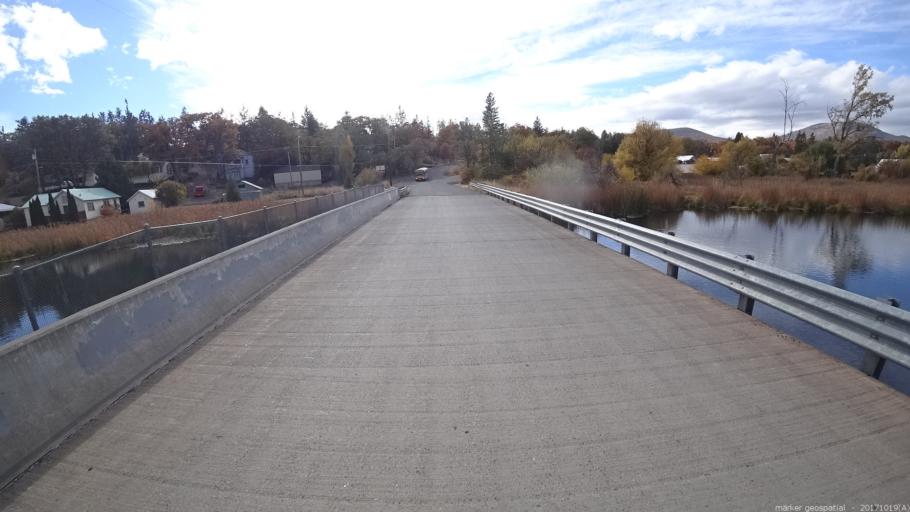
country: US
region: California
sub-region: Shasta County
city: Burney
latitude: 41.0015
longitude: -121.4403
